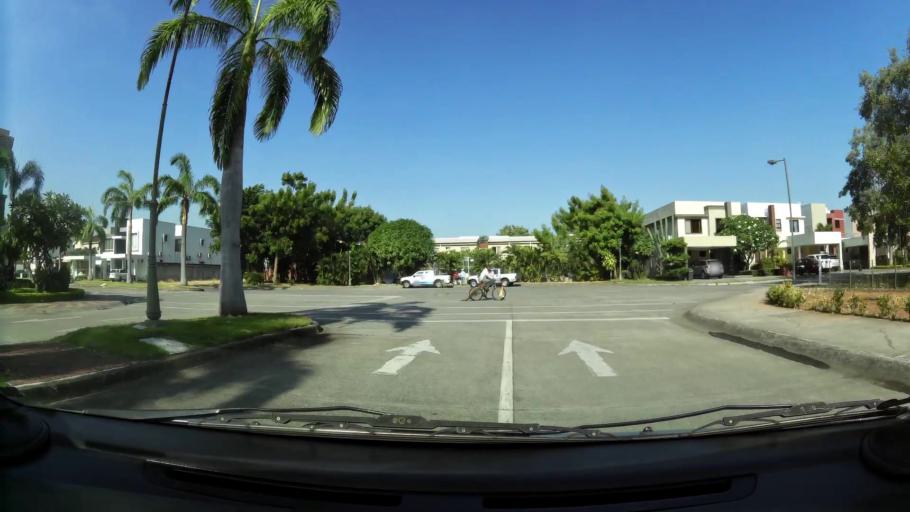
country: EC
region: Guayas
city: Santa Lucia
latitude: -2.1883
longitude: -79.9859
